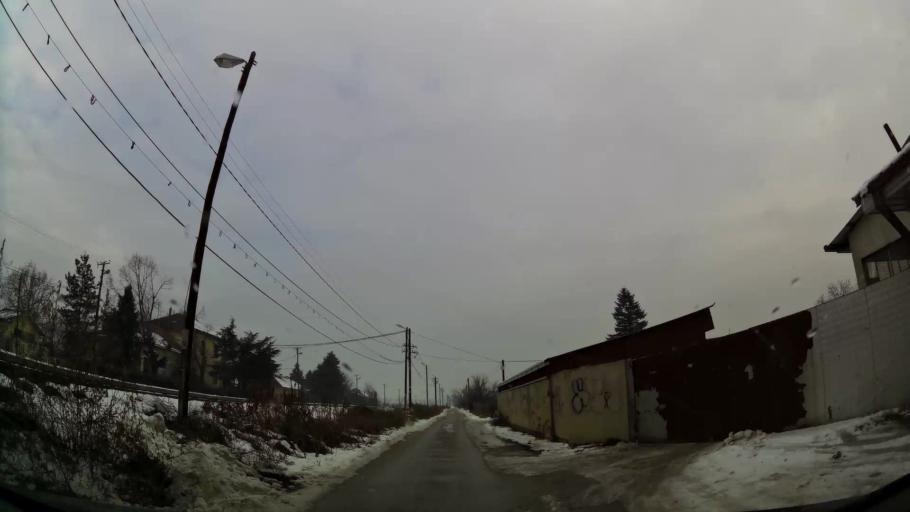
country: MK
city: Kondovo
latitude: 42.0466
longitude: 21.3541
